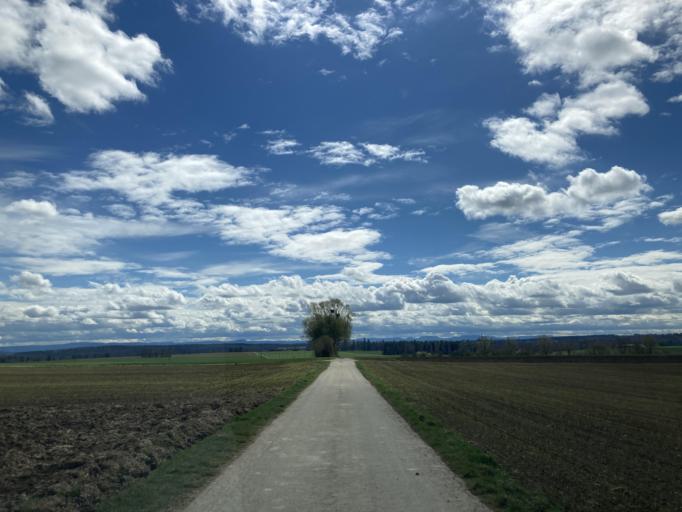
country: DE
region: Baden-Wuerttemberg
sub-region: Regierungsbezirk Stuttgart
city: Bondorf
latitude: 48.4658
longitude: 8.8161
